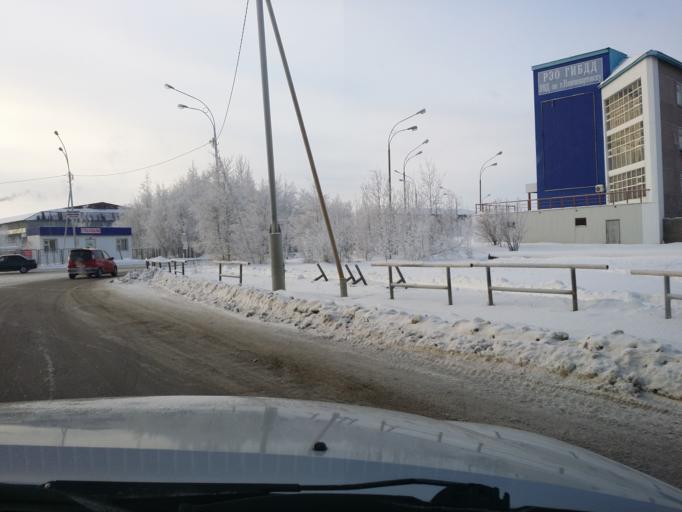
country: RU
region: Khanty-Mansiyskiy Avtonomnyy Okrug
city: Nizhnevartovsk
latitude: 60.9404
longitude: 76.5300
